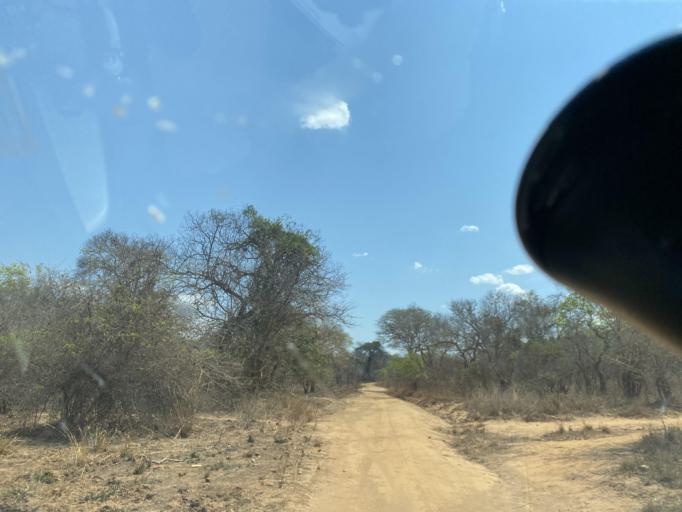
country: ZM
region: Lusaka
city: Chongwe
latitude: -15.0862
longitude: 29.4979
